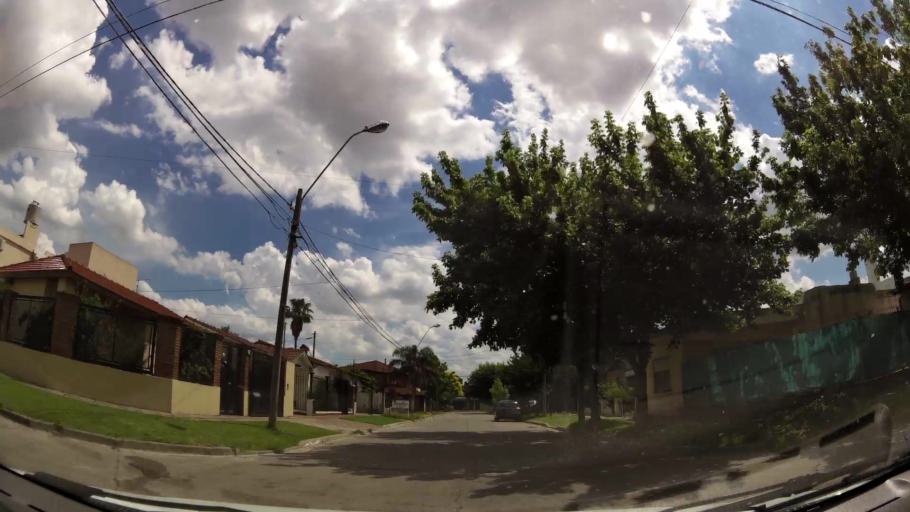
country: AR
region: Buenos Aires
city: Ituzaingo
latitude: -34.6535
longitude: -58.6785
